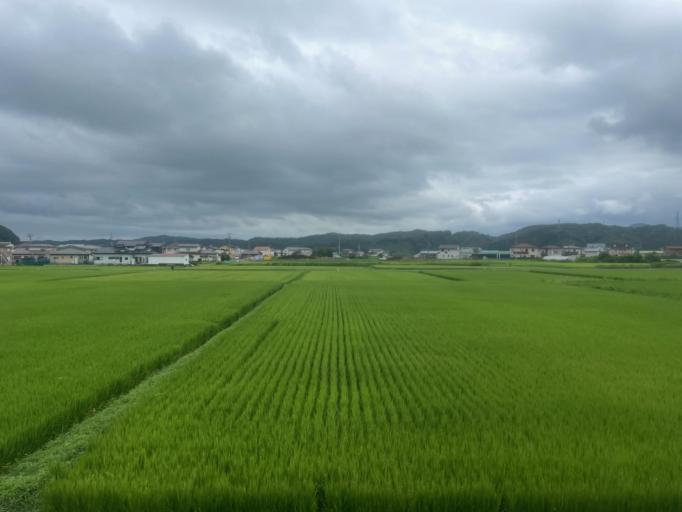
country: JP
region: Fukushima
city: Ishikawa
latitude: 37.1265
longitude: 140.2415
